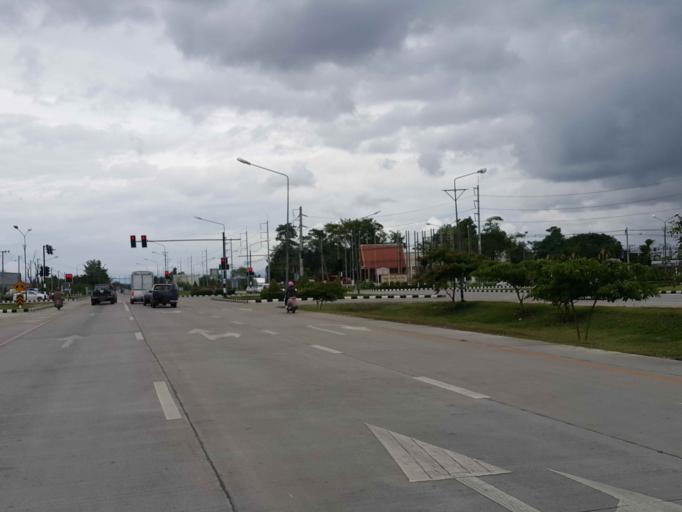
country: TH
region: Chiang Mai
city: San Kamphaeng
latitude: 18.7704
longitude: 99.0674
